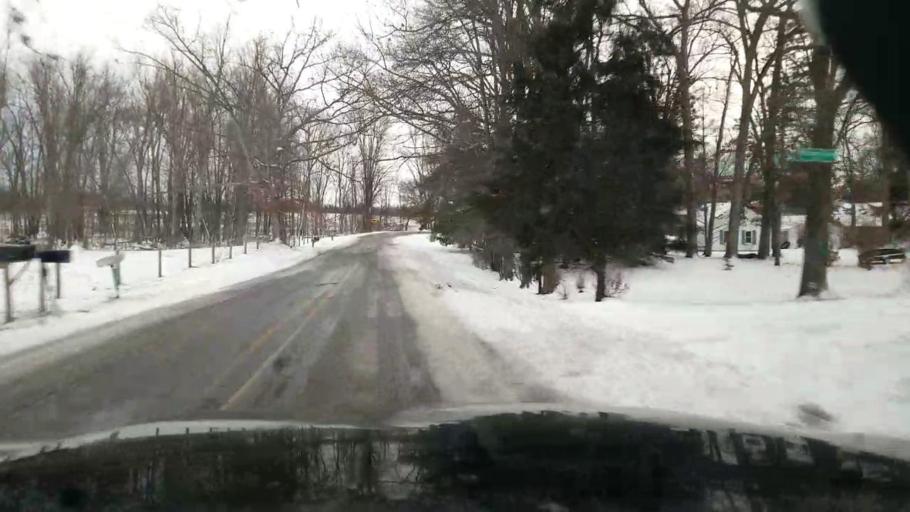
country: US
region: Michigan
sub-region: Jackson County
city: Vandercook Lake
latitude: 42.0887
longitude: -84.4658
